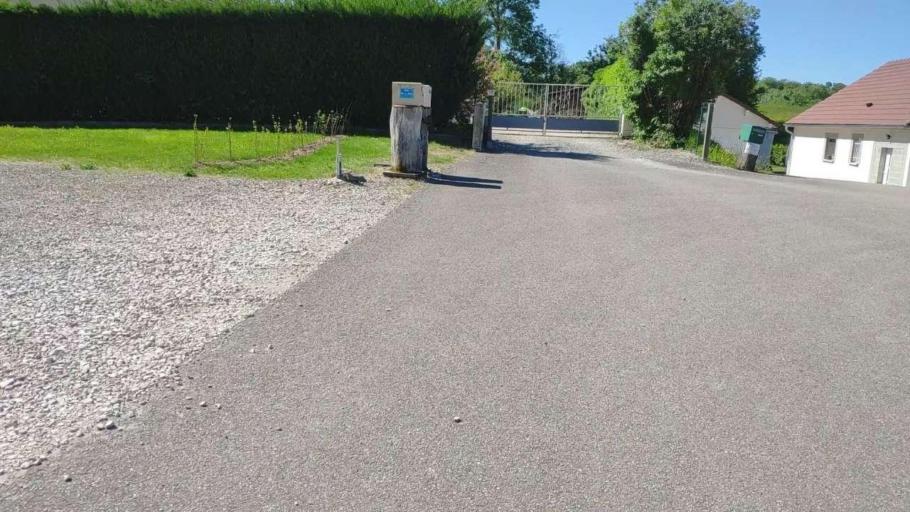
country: FR
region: Franche-Comte
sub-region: Departement du Jura
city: Clairvaux-les-Lacs
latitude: 46.6989
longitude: 5.7231
